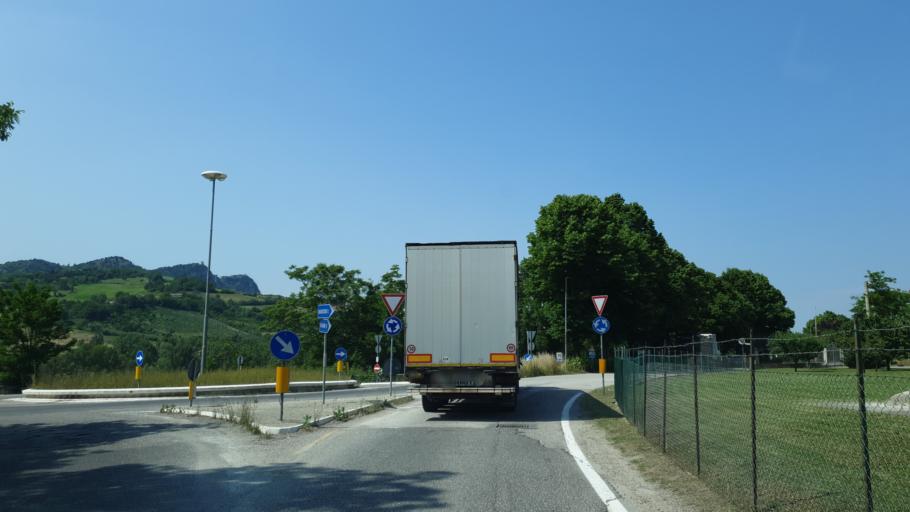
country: SM
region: Acquaviva
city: Acquaviva
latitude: 43.9611
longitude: 12.4019
